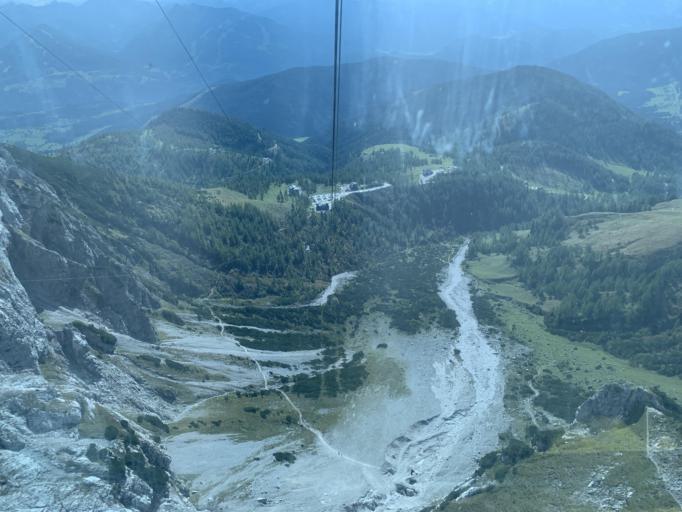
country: AT
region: Styria
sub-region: Politischer Bezirk Liezen
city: Schladming
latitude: 47.4611
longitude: 13.6228
